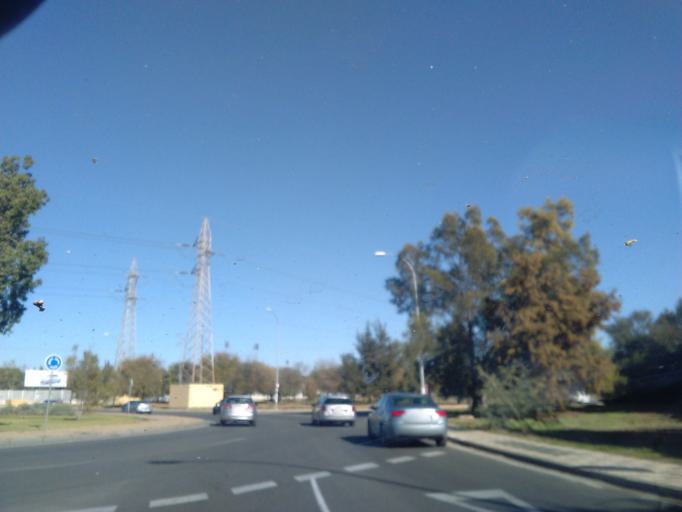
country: ES
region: Andalusia
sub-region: Provincia de Sevilla
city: Sevilla
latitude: 37.3895
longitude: -5.9142
